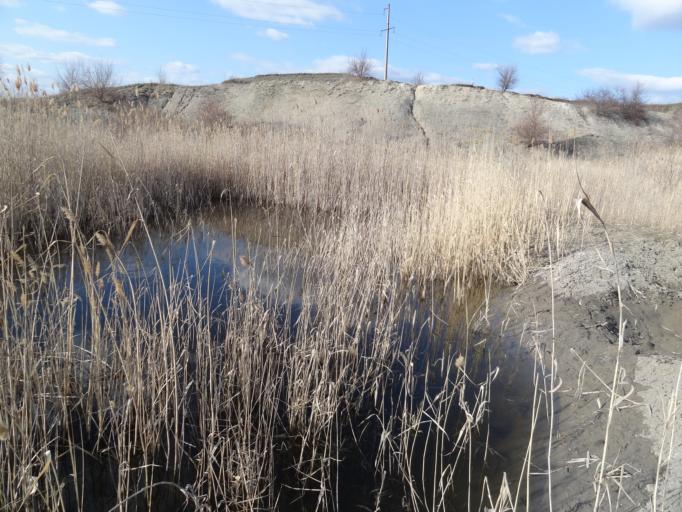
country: RU
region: Saratov
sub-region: Saratovskiy Rayon
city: Saratov
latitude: 51.6709
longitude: 46.0208
